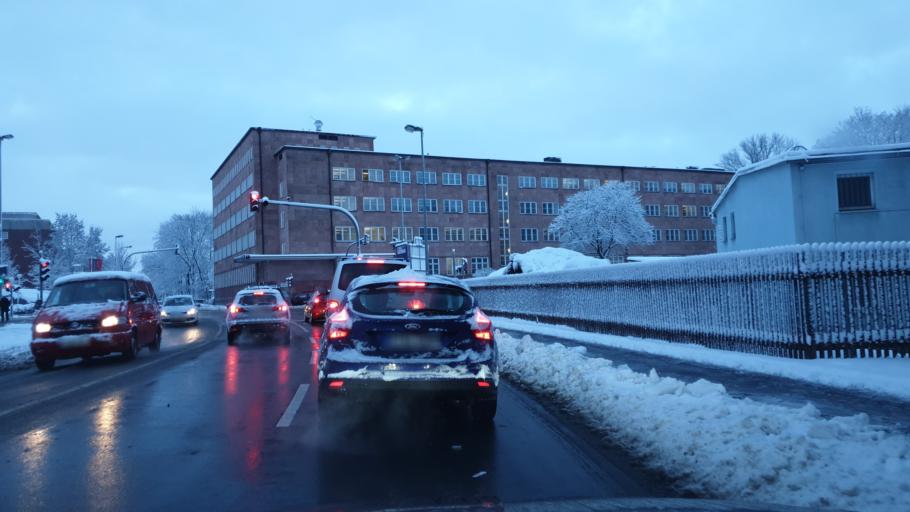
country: DE
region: Saxony
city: Chemnitz
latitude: 50.8457
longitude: 12.9195
